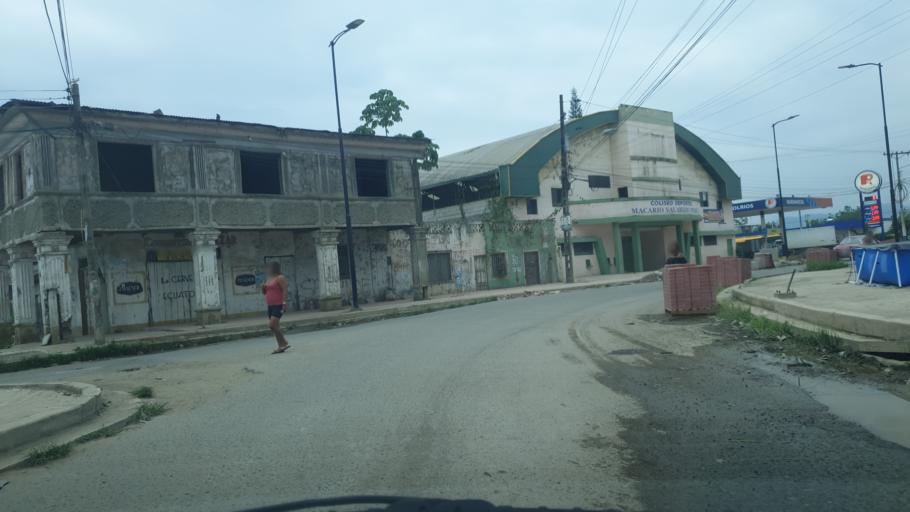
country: EC
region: El Oro
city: Pasaje
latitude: -3.3623
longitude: -79.8424
